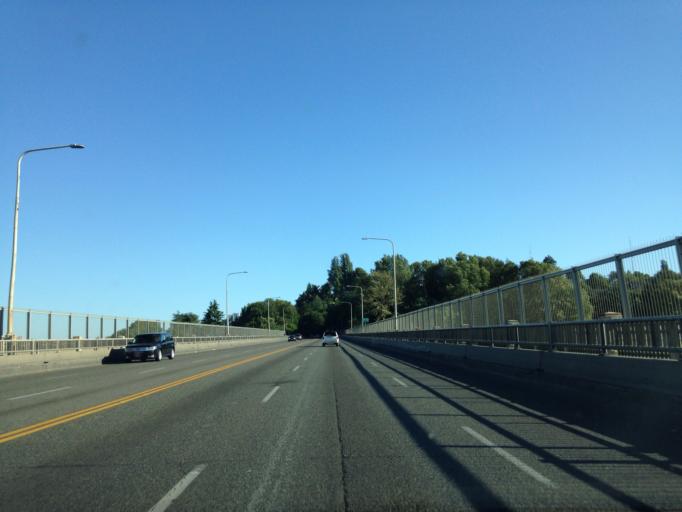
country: US
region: Washington
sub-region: King County
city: Seattle
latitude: 47.6459
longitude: -122.3474
